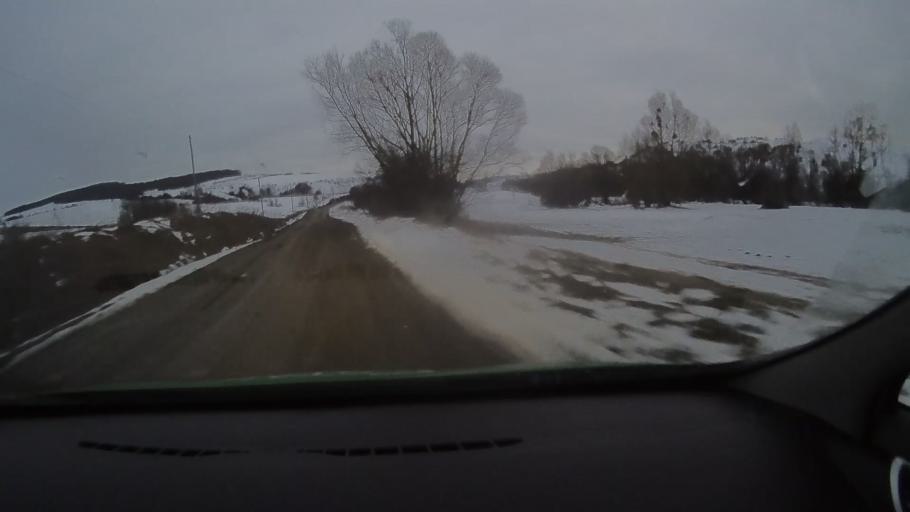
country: RO
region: Harghita
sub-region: Comuna Darjiu
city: Darjiu
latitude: 46.2075
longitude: 25.2429
